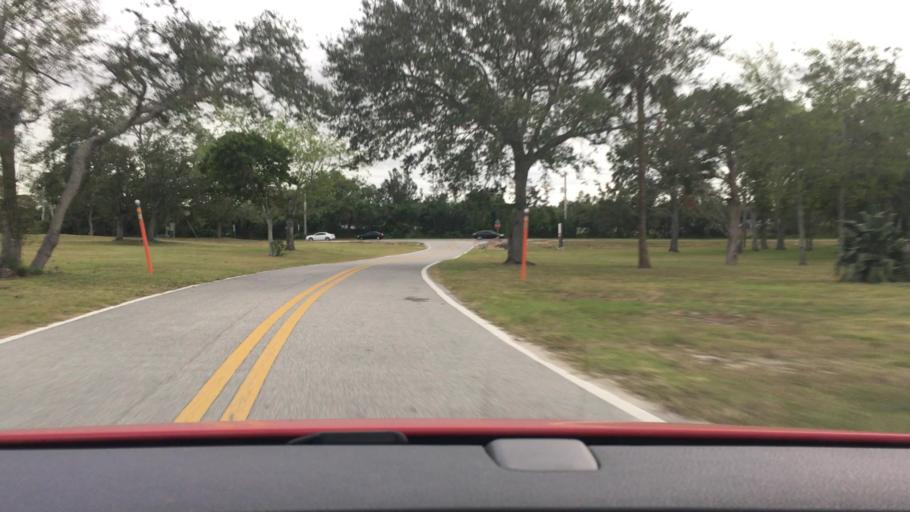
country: US
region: Florida
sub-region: Volusia County
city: Daytona Beach
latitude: 29.2054
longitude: -81.0562
